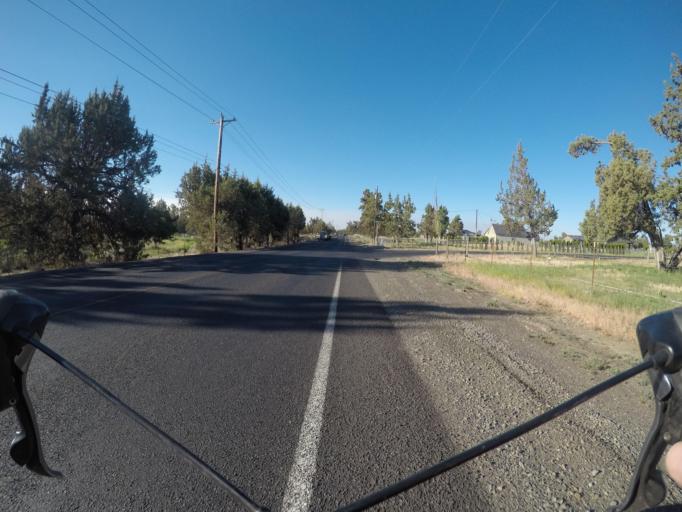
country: US
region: Oregon
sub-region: Deschutes County
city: Redmond
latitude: 44.2280
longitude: -121.2297
